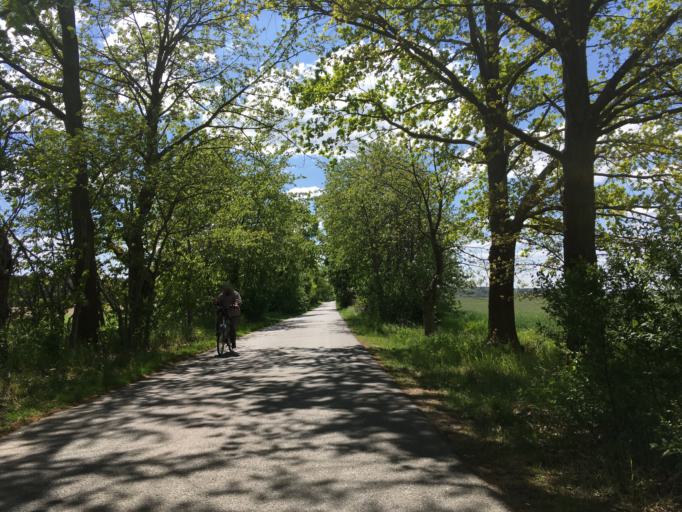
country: DE
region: Brandenburg
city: Rudnitz
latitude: 52.7300
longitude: 13.6642
